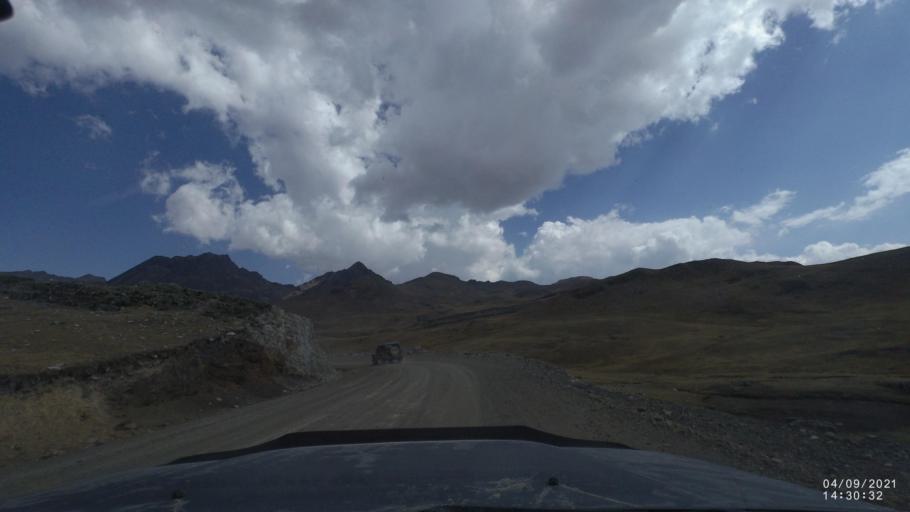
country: BO
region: Cochabamba
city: Sipe Sipe
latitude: -17.2450
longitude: -66.3959
